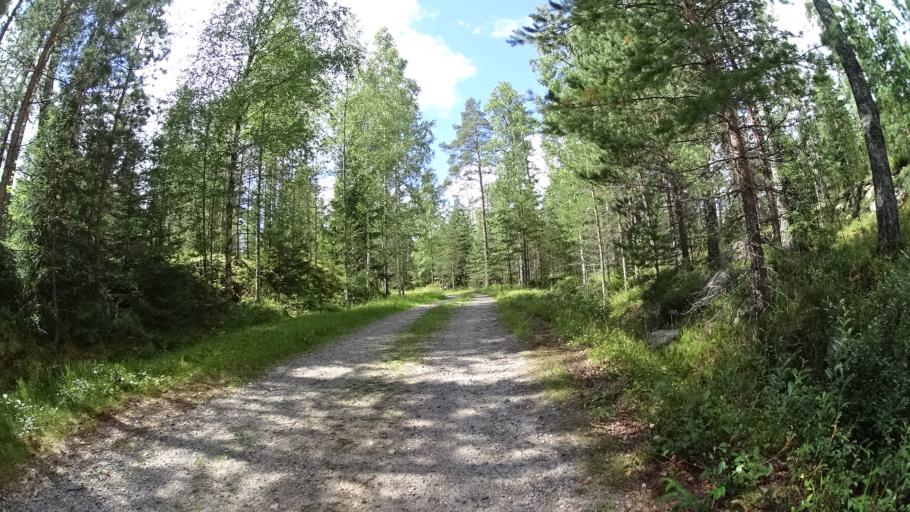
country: FI
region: Uusimaa
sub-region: Helsinki
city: Espoo
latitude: 60.3474
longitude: 24.6681
